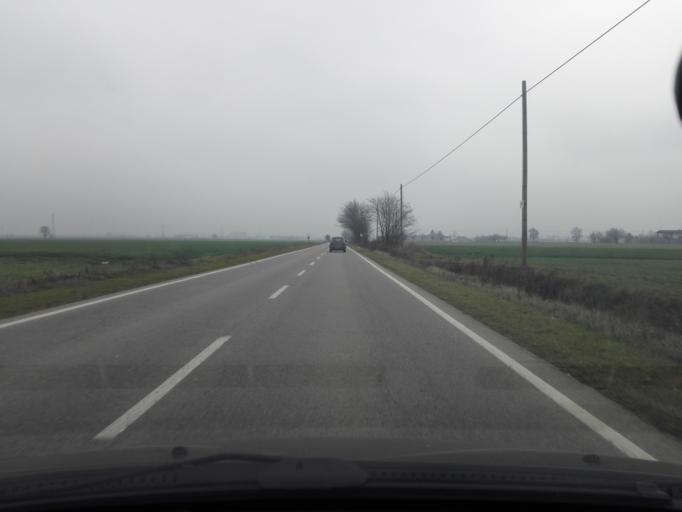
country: IT
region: Piedmont
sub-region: Provincia di Alessandria
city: Fresonara
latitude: 44.8033
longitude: 8.7113
